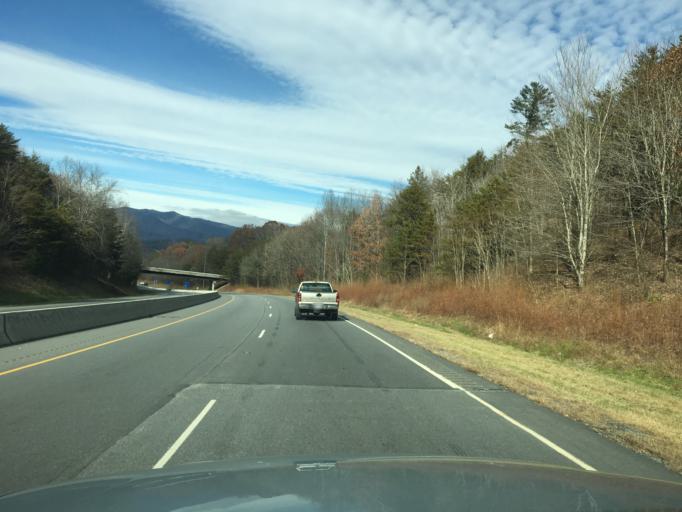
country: US
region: North Carolina
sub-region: McDowell County
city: Marion
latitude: 35.6968
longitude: -82.0301
